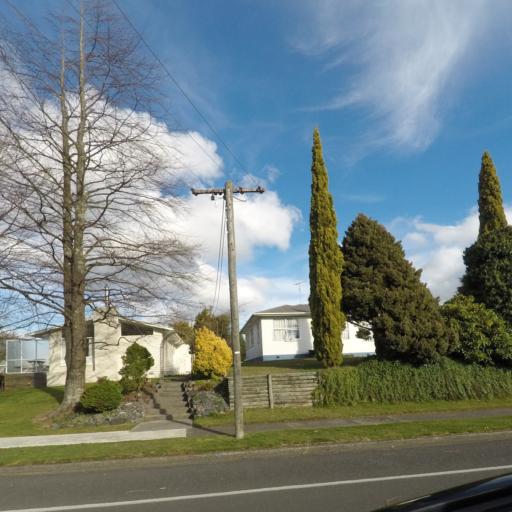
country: NZ
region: Manawatu-Wanganui
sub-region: Ruapehu District
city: Waiouru
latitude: -39.4138
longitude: 175.4030
